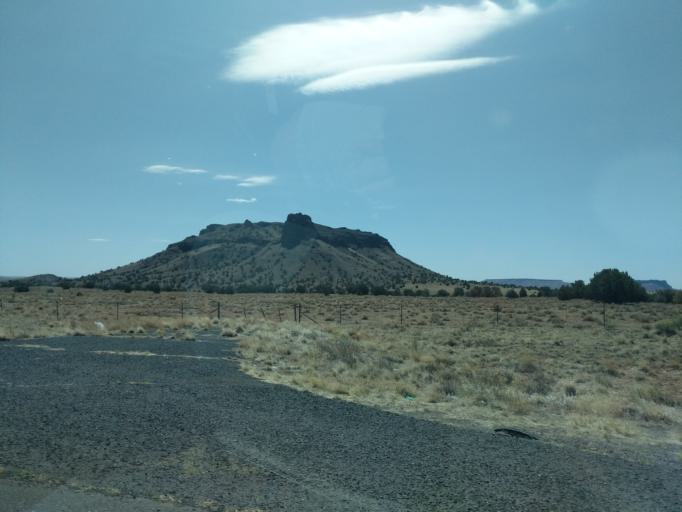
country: US
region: Arizona
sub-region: Navajo County
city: Dilkon
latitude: 35.3911
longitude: -110.0945
